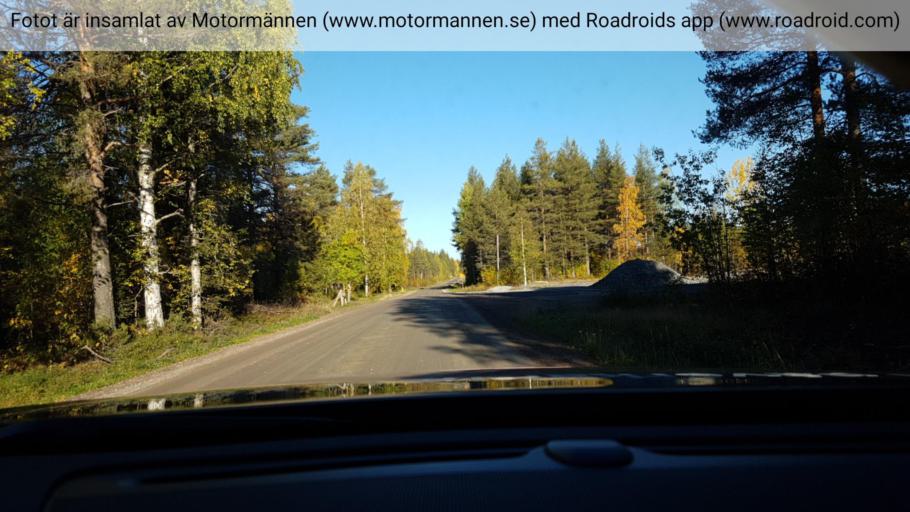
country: SE
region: Norrbotten
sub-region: Alvsbyns Kommun
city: AElvsbyn
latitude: 66.1976
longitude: 21.1852
